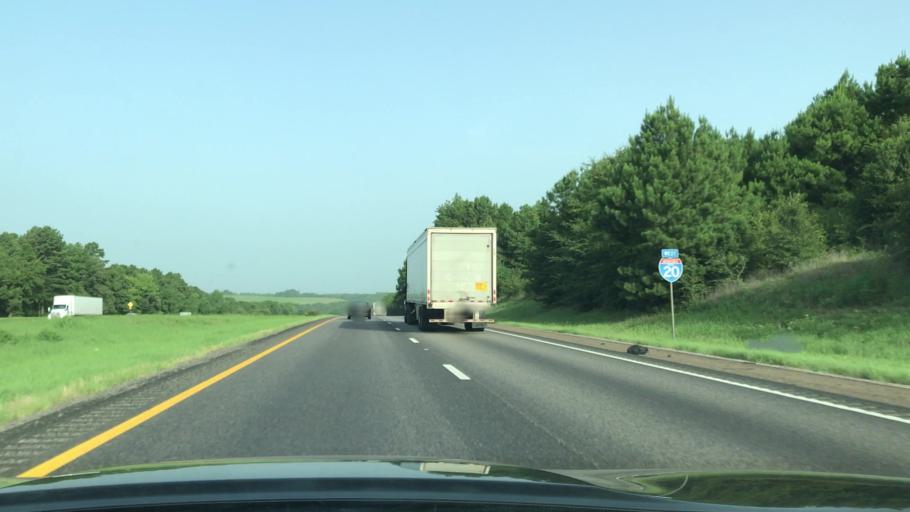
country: US
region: Texas
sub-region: Smith County
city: Tyler
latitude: 32.4548
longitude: -95.2929
